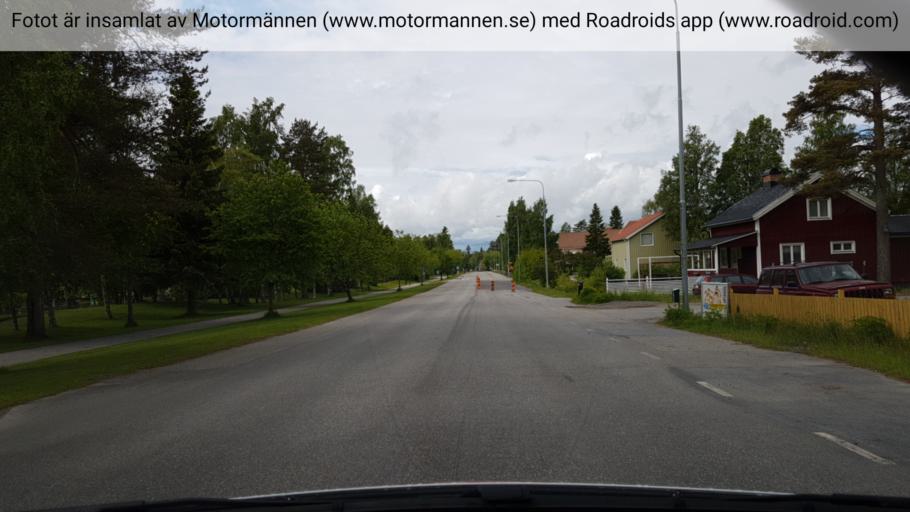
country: SE
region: Vaesterbotten
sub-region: Umea Kommun
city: Hoernefors
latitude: 63.6252
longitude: 19.9161
